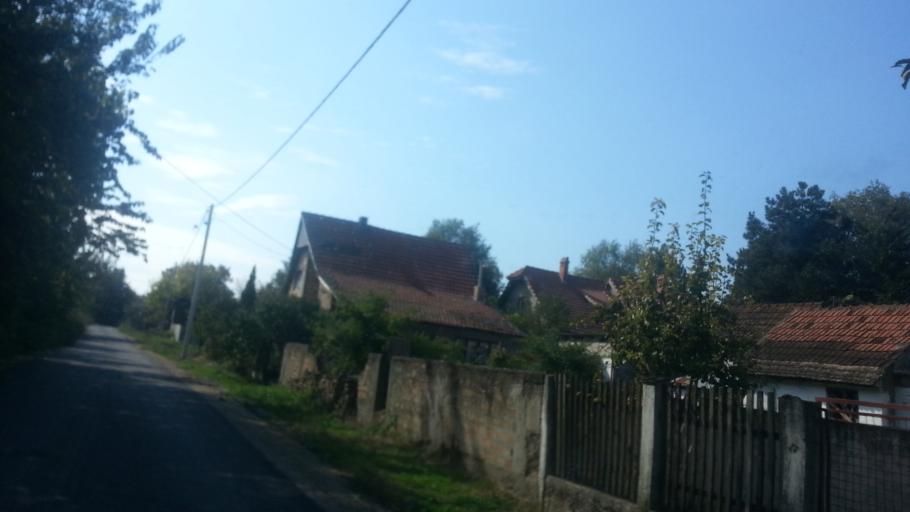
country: RS
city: Surduk
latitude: 45.0842
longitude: 20.3091
